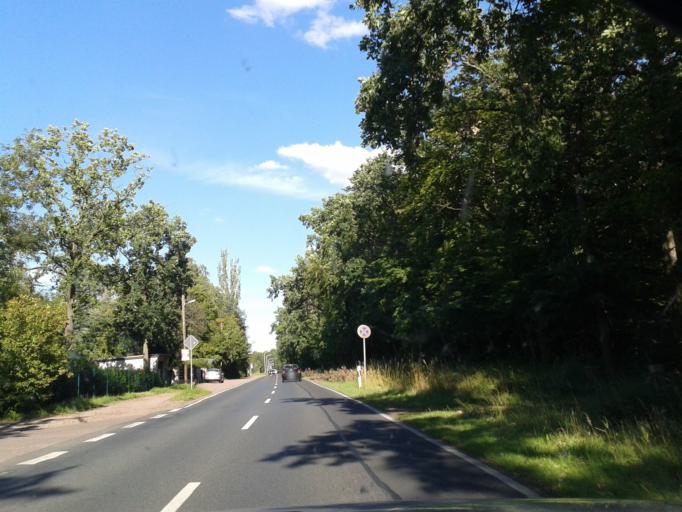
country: DE
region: Saxony-Anhalt
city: Halle Neustadt
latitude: 51.5107
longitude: 11.9135
